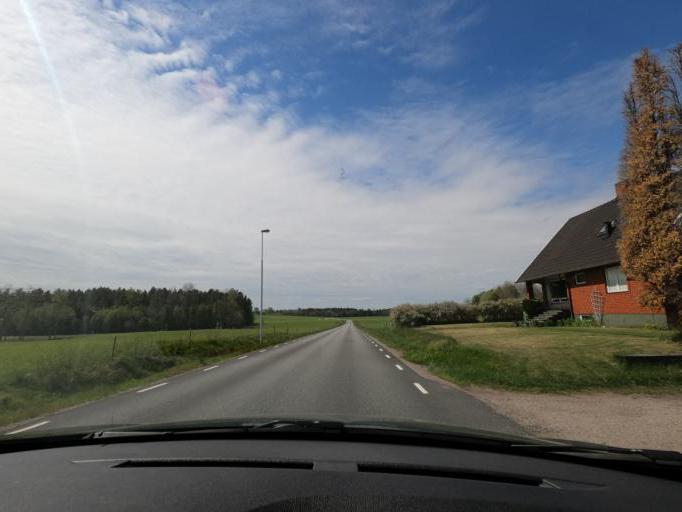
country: SE
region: Joenkoeping
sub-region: Varnamo Kommun
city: Bredaryd
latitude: 57.1303
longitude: 13.6980
